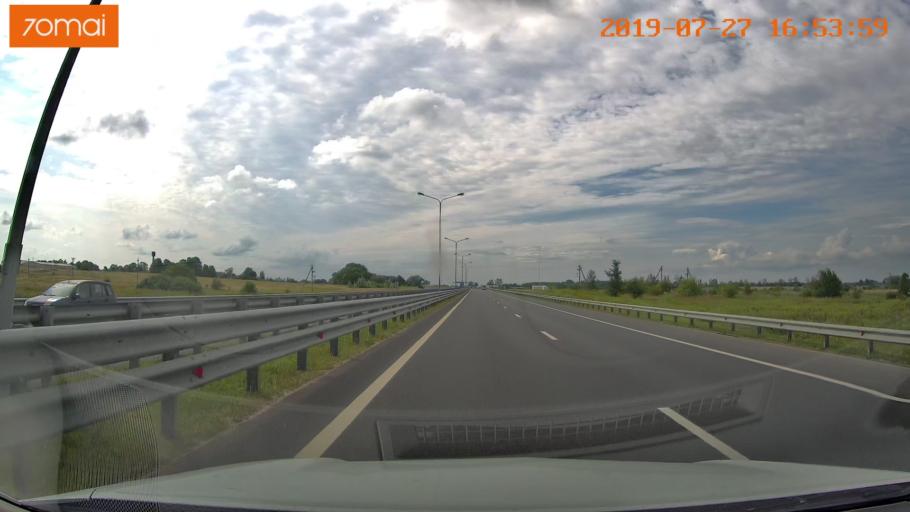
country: RU
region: Kaliningrad
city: Bol'shoe Isakovo
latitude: 54.6918
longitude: 20.8189
